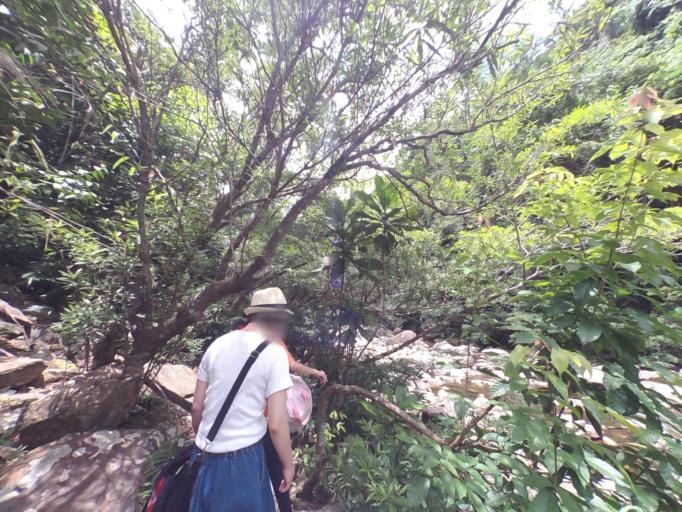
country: VN
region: Thua Thien-Hue
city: A Luoi
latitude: 16.3053
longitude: 107.3244
